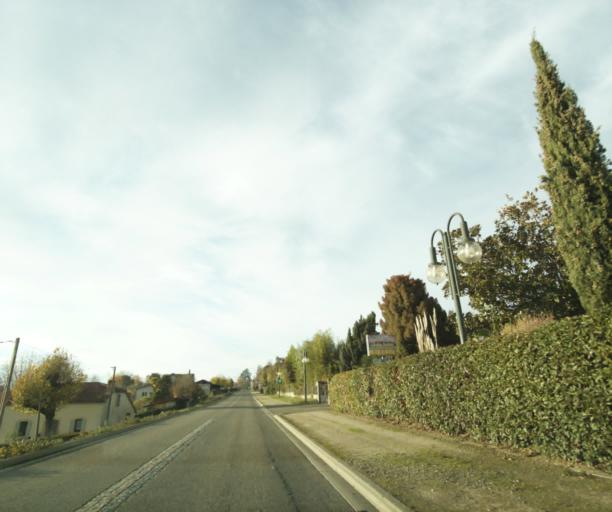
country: FR
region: Midi-Pyrenees
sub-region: Departement du Gers
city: Cazaubon
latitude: 43.9327
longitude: -0.0550
